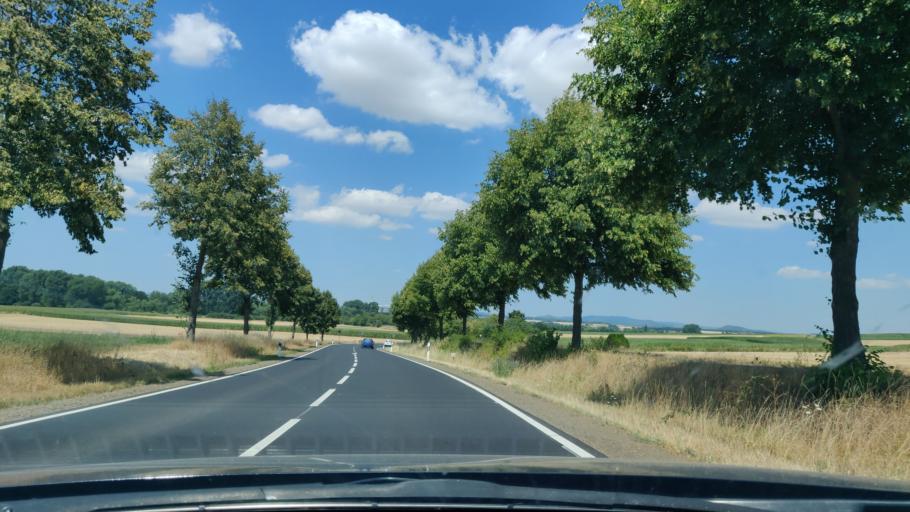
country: DE
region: Hesse
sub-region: Regierungsbezirk Kassel
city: Wabern
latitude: 51.0857
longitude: 9.3736
